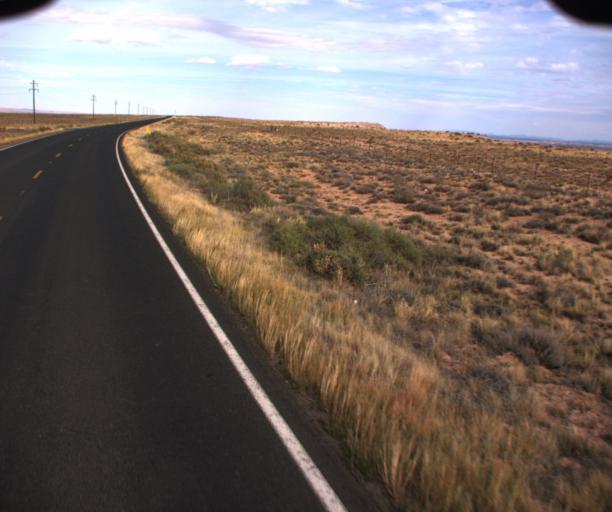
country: US
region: Arizona
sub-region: Apache County
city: Ganado
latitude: 35.9018
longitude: -109.6112
